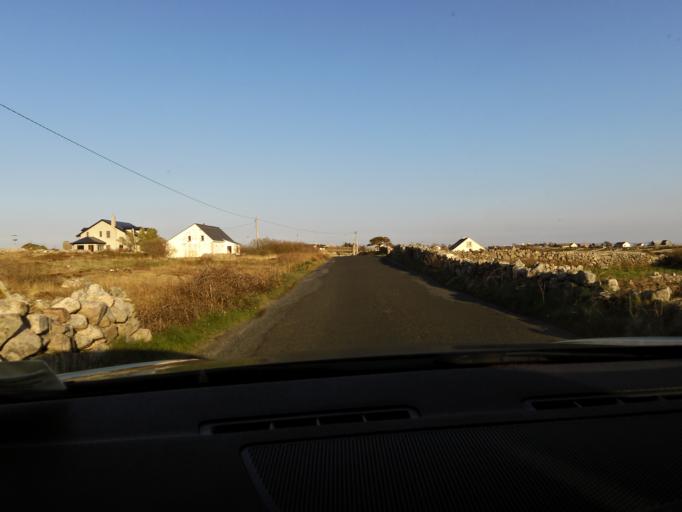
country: IE
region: Connaught
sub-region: County Galway
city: Oughterard
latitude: 53.2461
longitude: -9.5314
